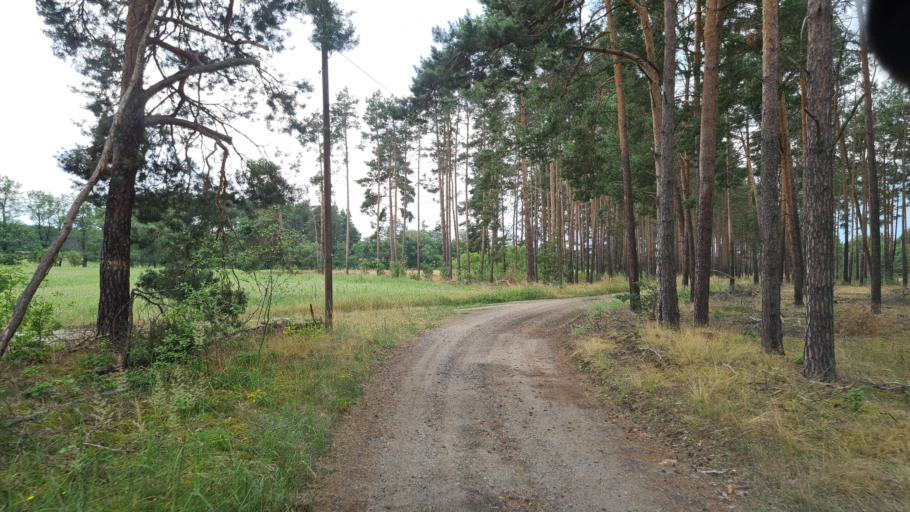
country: DE
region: Brandenburg
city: Crinitz
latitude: 51.6646
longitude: 13.7937
